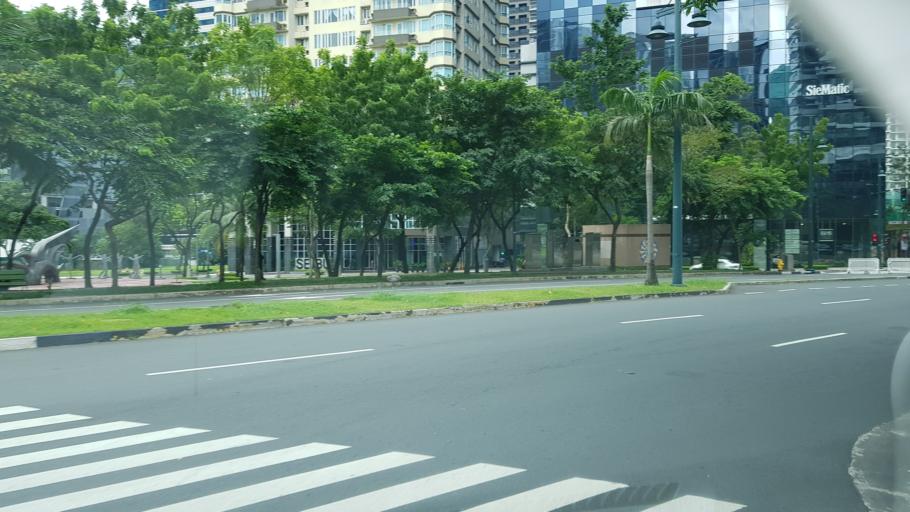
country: PH
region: Metro Manila
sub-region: Makati City
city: Makati City
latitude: 14.5462
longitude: 121.0477
